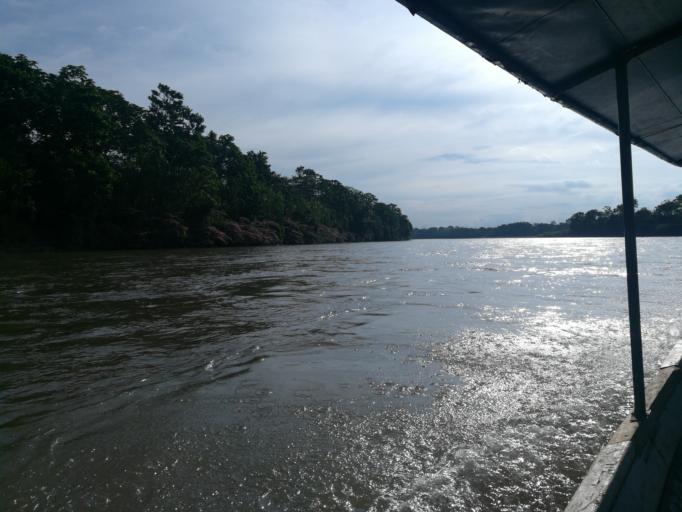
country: EC
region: Orellana
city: Boca Suno
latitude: -0.8513
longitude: -77.2363
